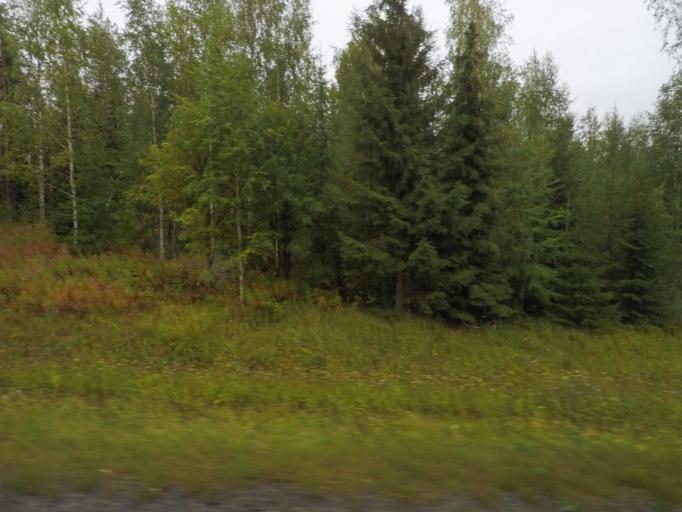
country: FI
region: Southern Savonia
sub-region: Pieksaemaeki
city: Juva
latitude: 62.0083
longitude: 27.8014
